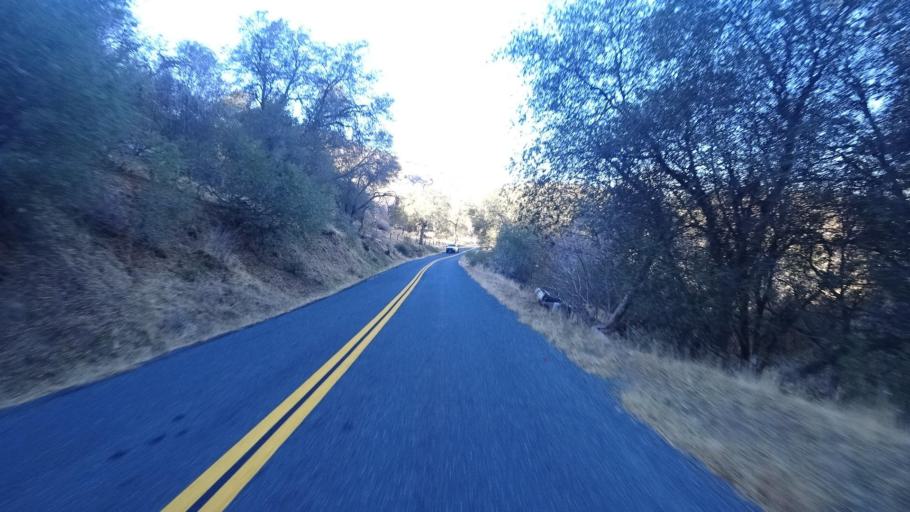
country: US
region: California
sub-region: Kern County
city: Alta Sierra
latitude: 35.7873
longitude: -118.7542
